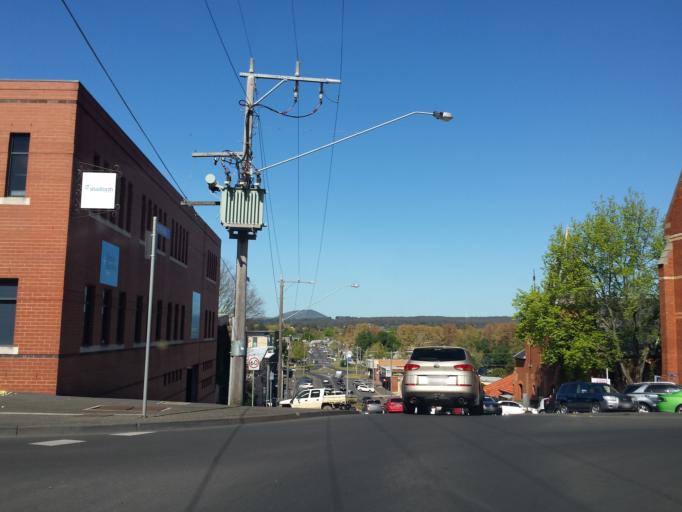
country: AU
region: Victoria
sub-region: Ballarat North
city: Ballarat Central
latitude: -37.5641
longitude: 143.8574
